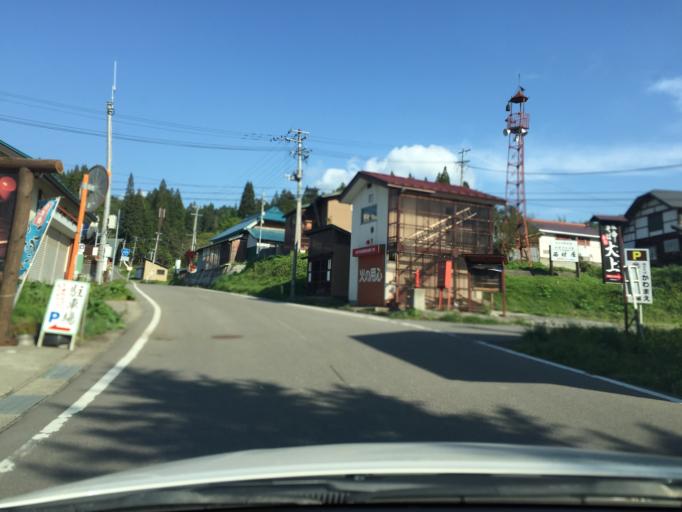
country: JP
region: Fukushima
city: Kitakata
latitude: 37.6935
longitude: 139.7154
